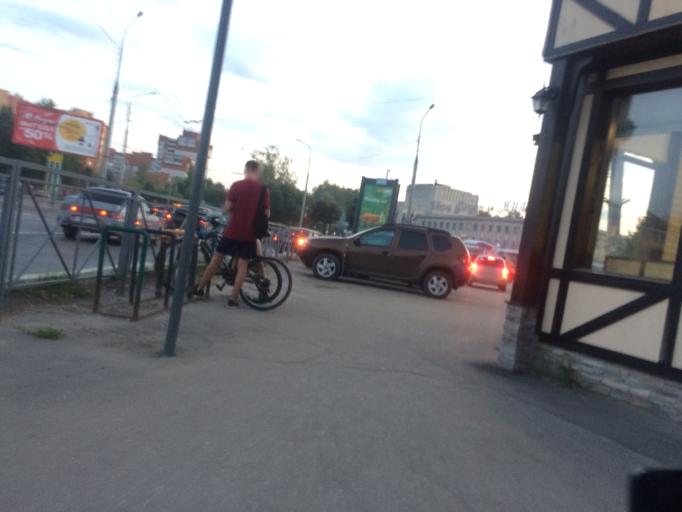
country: RU
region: Mariy-El
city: Yoshkar-Ola
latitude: 56.6408
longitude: 47.8716
